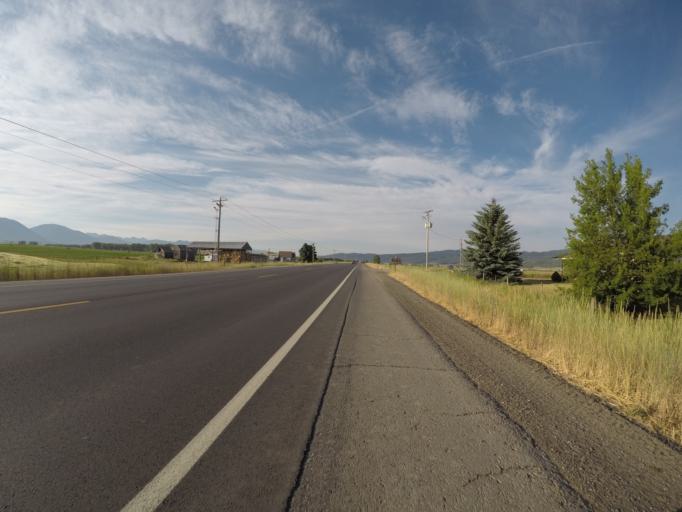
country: US
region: Wyoming
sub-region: Lincoln County
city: Afton
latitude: 42.9612
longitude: -111.0124
